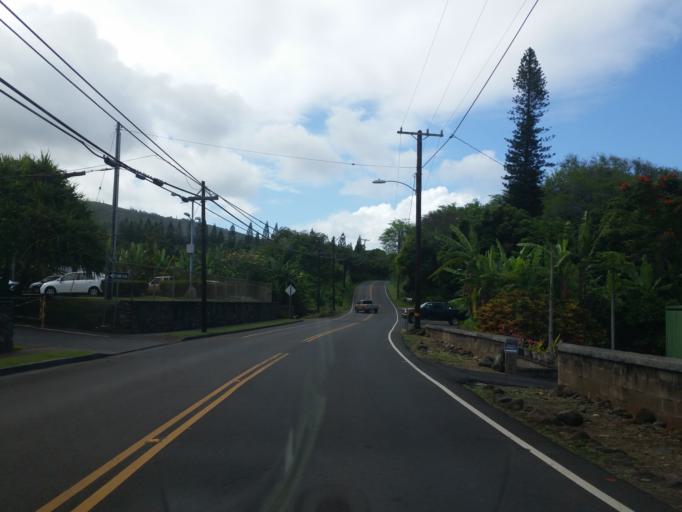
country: US
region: Hawaii
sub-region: Maui County
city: Waihee-Waiehu
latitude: 20.9344
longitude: -156.5132
